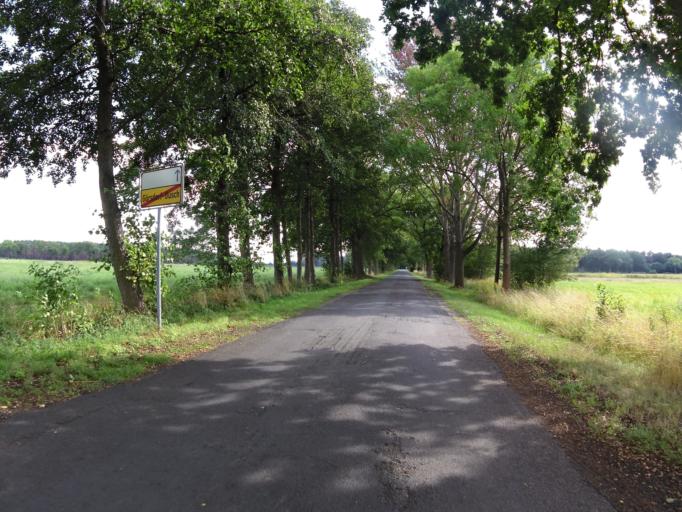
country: DE
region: Brandenburg
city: Storkow
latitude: 52.2352
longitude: 13.8721
